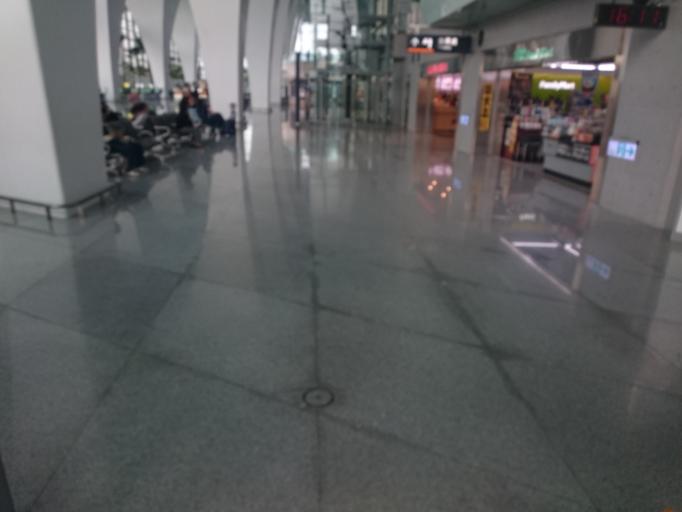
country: TW
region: Taiwan
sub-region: Nantou
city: Nantou
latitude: 23.8741
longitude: 120.5742
